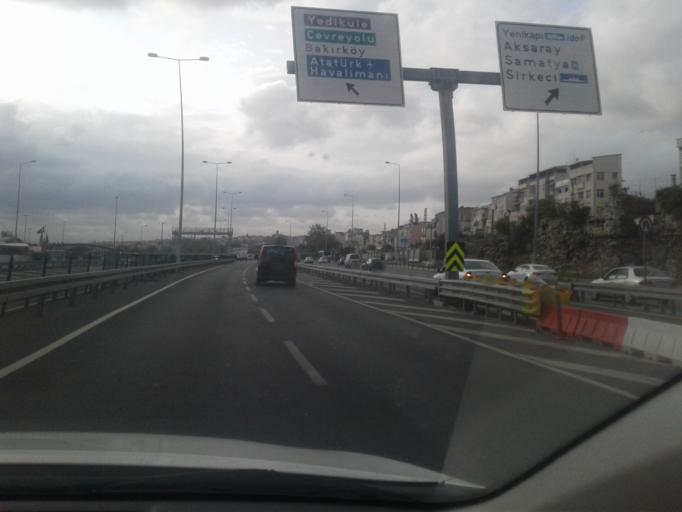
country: TR
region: Istanbul
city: Istanbul
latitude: 41.0031
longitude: 28.9615
